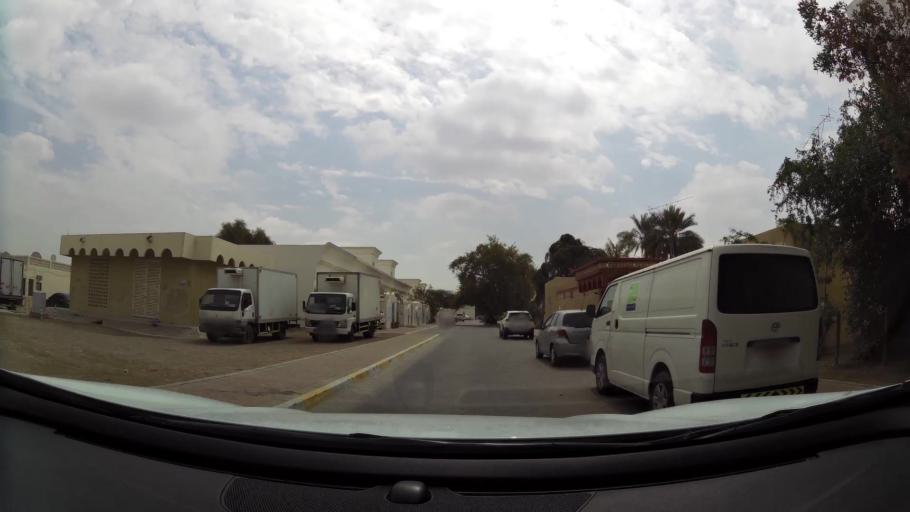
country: AE
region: Abu Dhabi
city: Al Ain
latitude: 24.2193
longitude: 55.7771
